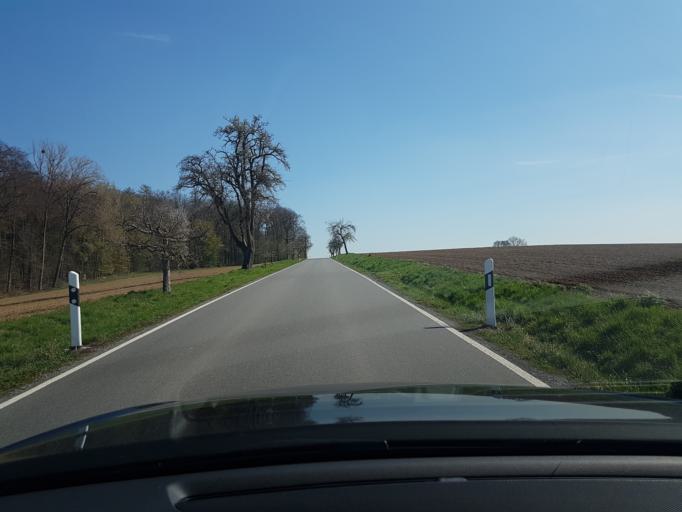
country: DE
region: Baden-Wuerttemberg
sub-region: Regierungsbezirk Stuttgart
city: Widdern
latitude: 49.2824
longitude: 9.4389
